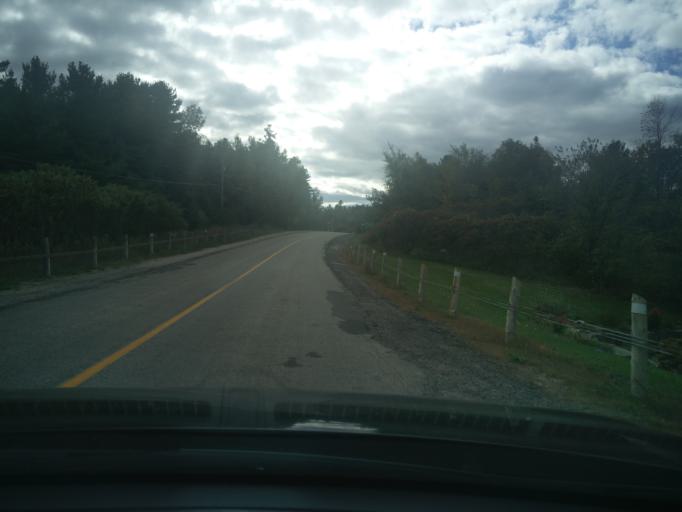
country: CA
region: Ontario
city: Perth
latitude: 44.6396
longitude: -76.5201
